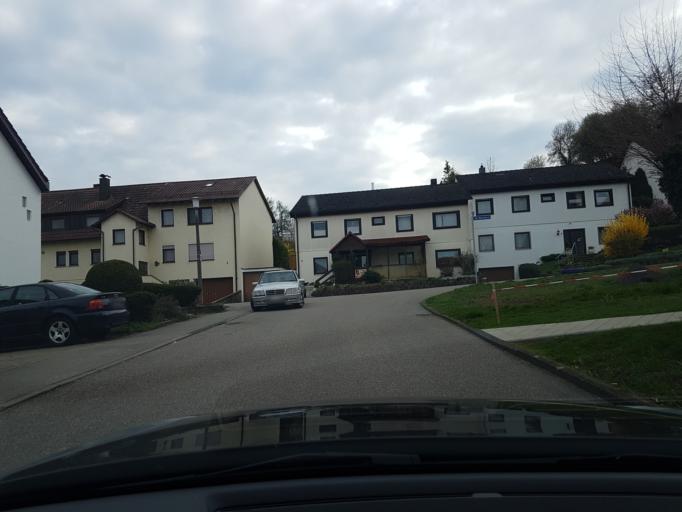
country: DE
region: Baden-Wuerttemberg
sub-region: Regierungsbezirk Stuttgart
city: Neuenstadt am Kocher
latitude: 49.2352
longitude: 9.3230
